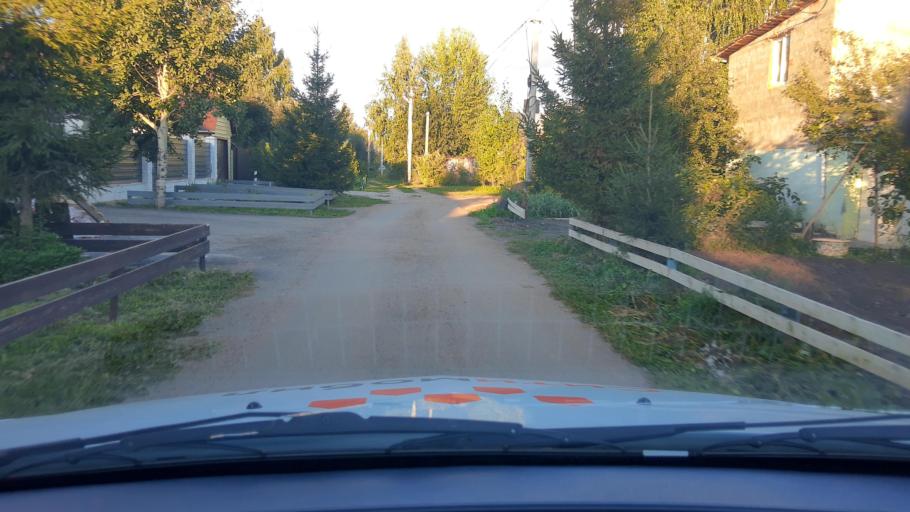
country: RU
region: Bashkortostan
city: Ufa
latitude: 54.6534
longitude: 56.0551
